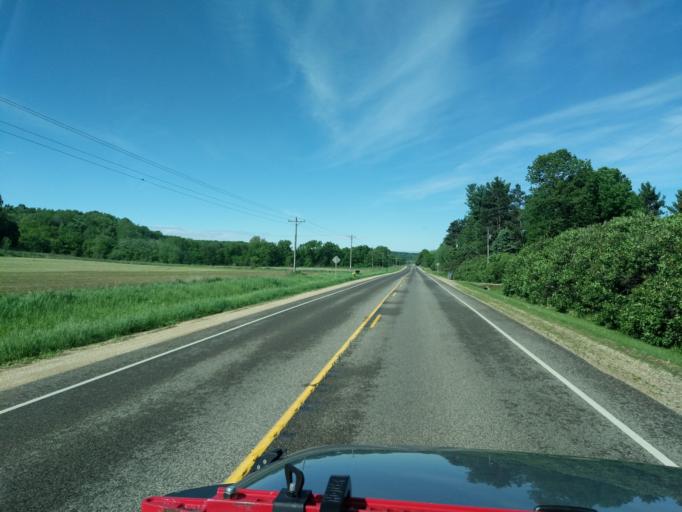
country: US
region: Wisconsin
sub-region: Pierce County
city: River Falls
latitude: 44.8584
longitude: -92.5311
